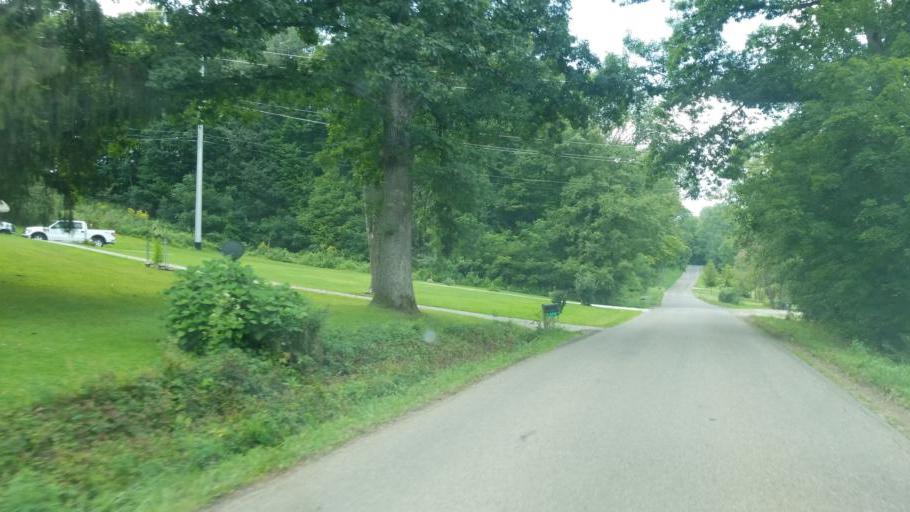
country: US
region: Ohio
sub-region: Knox County
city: Mount Vernon
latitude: 40.4257
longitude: -82.4641
